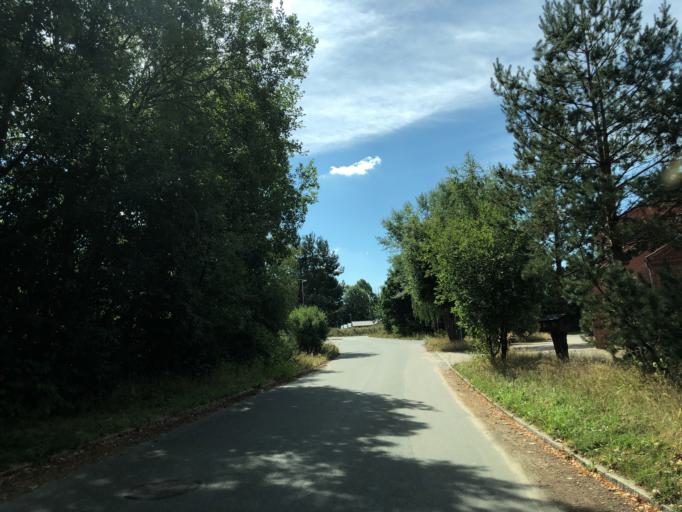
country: DK
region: Central Jutland
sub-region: Silkeborg Kommune
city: Silkeborg
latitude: 56.1600
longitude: 9.5012
